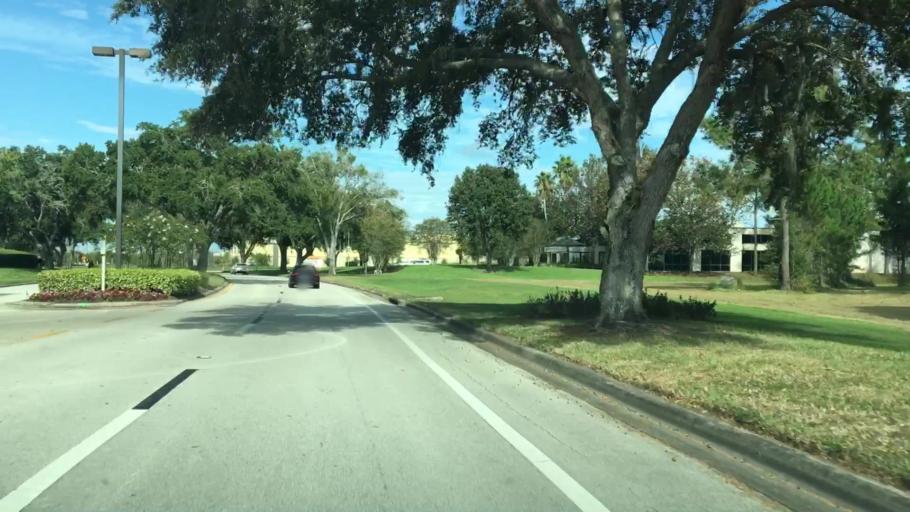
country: US
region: Florida
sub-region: Orange County
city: Conway
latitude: 28.4612
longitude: -81.3027
